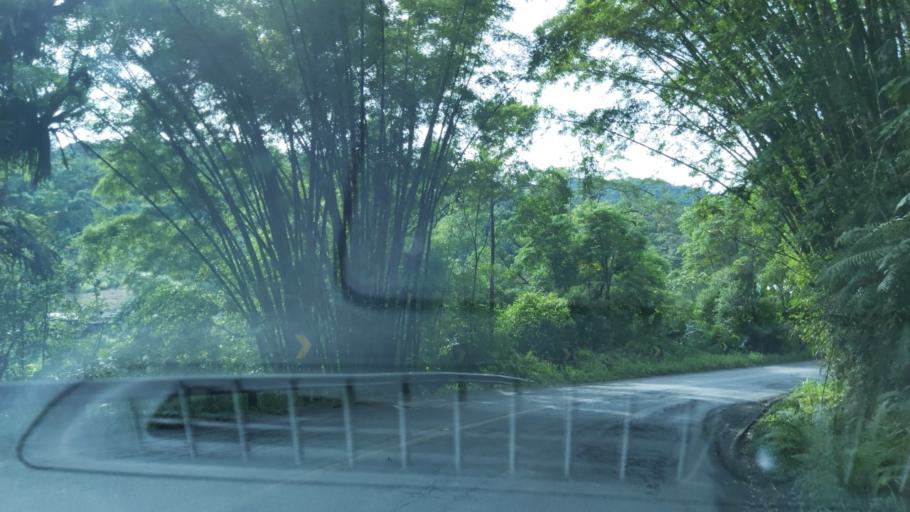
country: BR
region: Sao Paulo
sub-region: Miracatu
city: Miracatu
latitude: -24.0542
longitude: -47.5770
